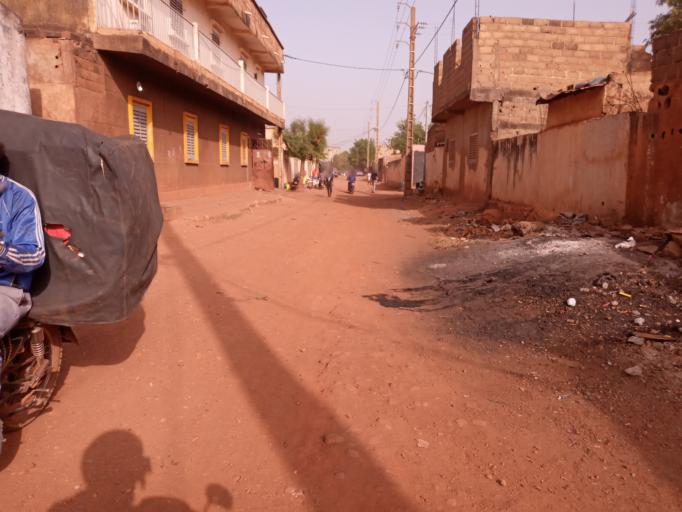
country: ML
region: Bamako
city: Bamako
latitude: 12.6008
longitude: -7.9660
